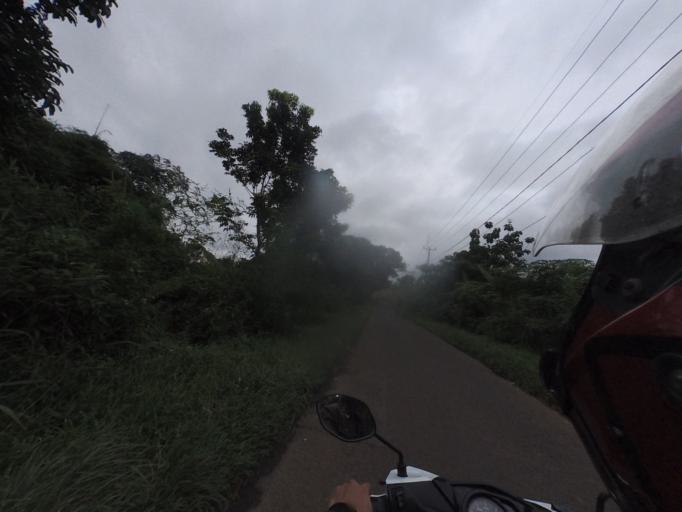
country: ID
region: West Java
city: Bogor
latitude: -6.6534
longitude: 106.7282
